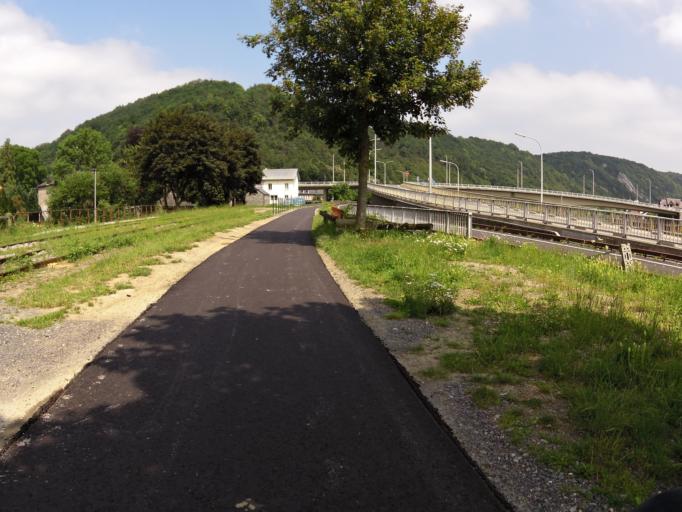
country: BE
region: Wallonia
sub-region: Province de Namur
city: Hastiere-Lavaux
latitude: 50.2151
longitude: 4.8247
